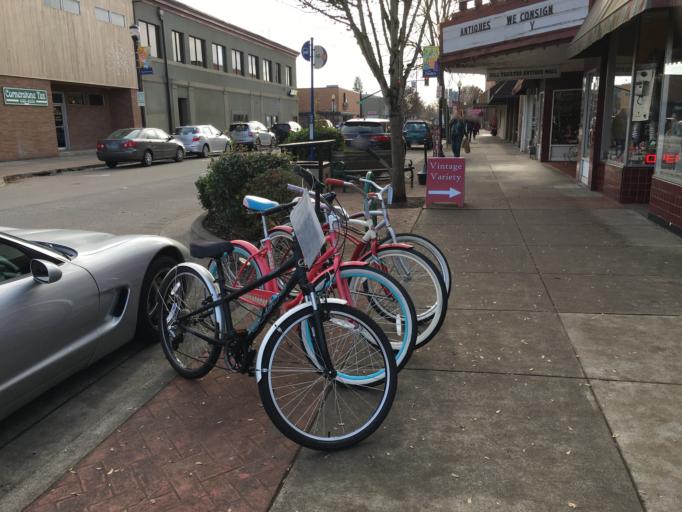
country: US
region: Oregon
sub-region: Washington County
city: Hillsboro
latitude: 45.5233
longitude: -122.9863
